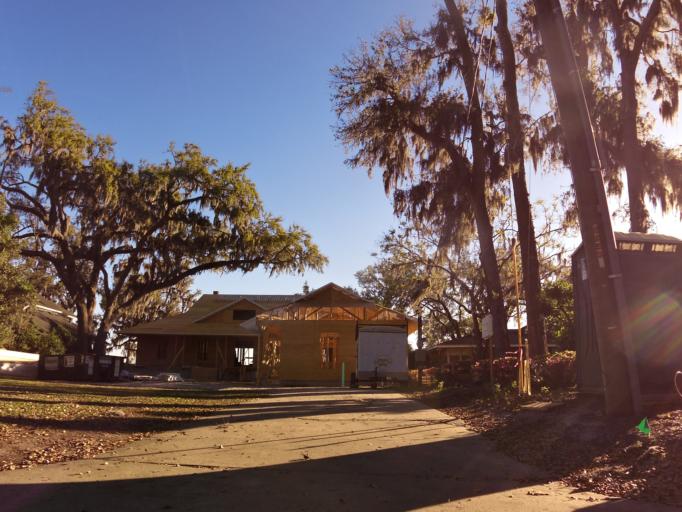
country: US
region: Florida
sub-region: Duval County
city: Jacksonville
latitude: 30.2469
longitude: -81.6375
